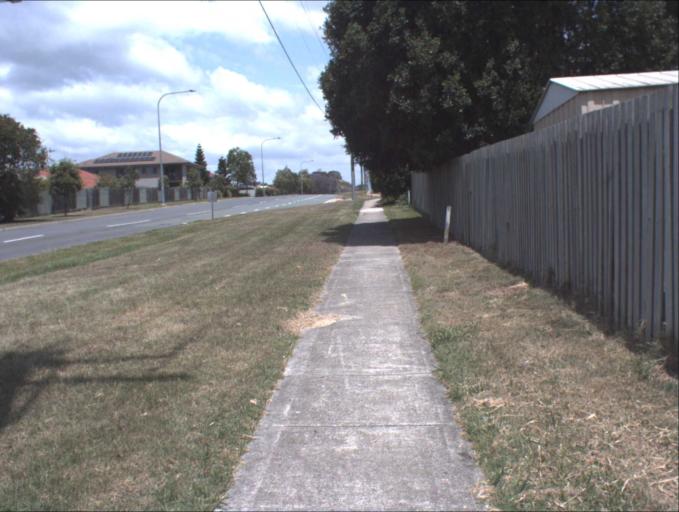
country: AU
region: Queensland
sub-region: Logan
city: Rochedale South
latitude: -27.5957
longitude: 153.1053
